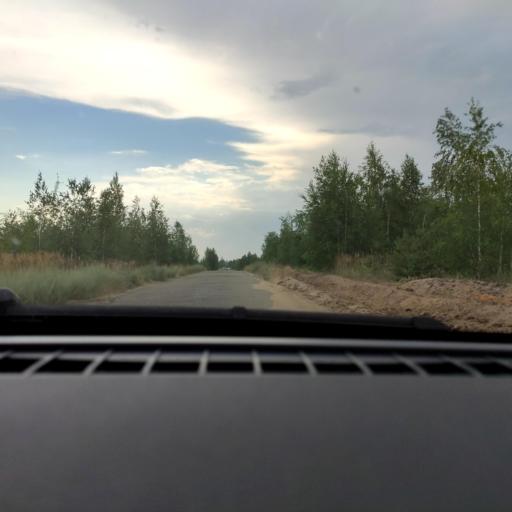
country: RU
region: Voronezj
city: Somovo
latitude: 51.7674
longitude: 39.3272
